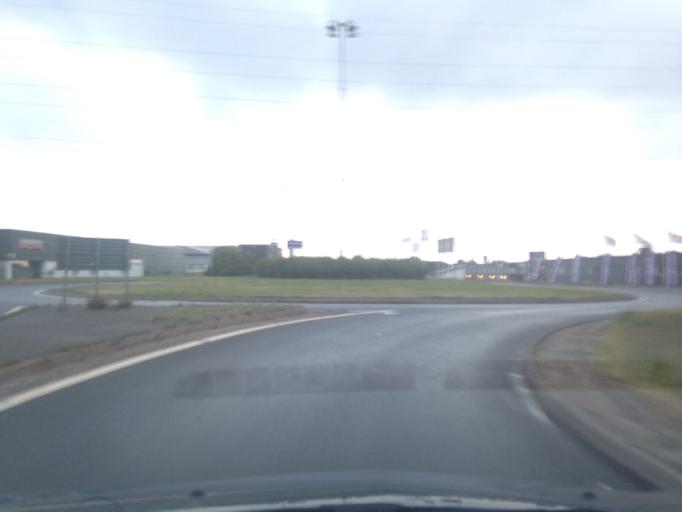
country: SE
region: Halland
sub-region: Varbergs Kommun
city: Varberg
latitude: 57.1232
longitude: 12.2888
